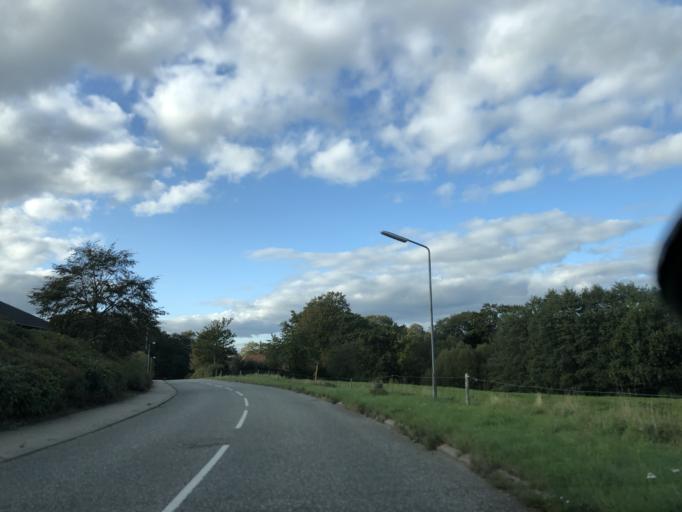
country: DK
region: Central Jutland
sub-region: Favrskov Kommune
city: Hammel
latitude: 56.2239
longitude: 9.7463
